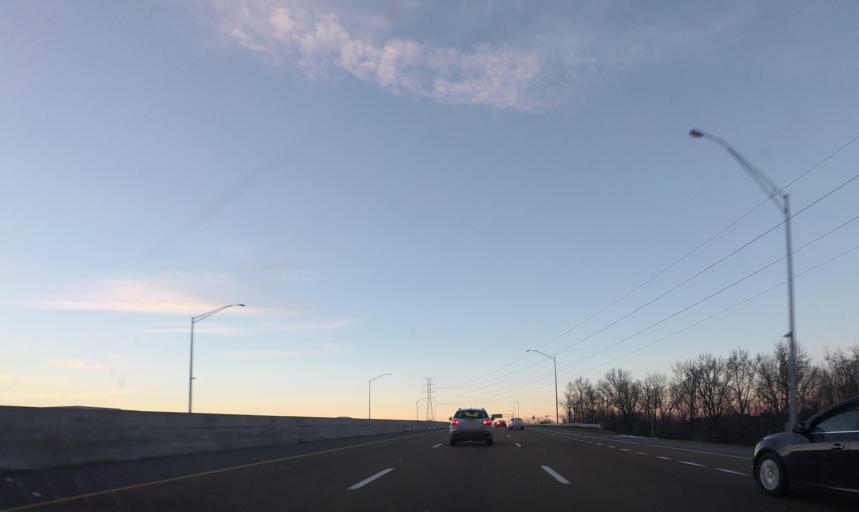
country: US
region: Tennessee
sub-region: Shelby County
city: Germantown
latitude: 35.0595
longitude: -89.8356
